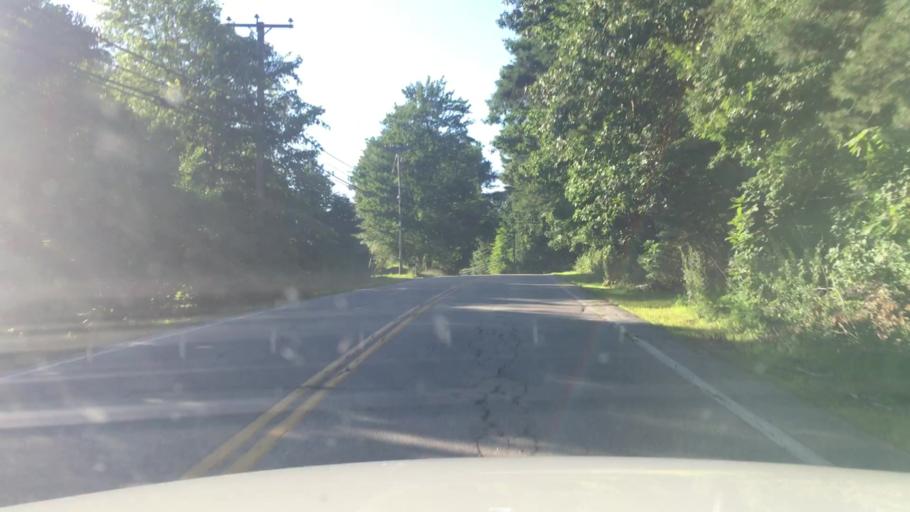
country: US
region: New Hampshire
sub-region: Rockingham County
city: Sandown
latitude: 42.9192
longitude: -71.1692
